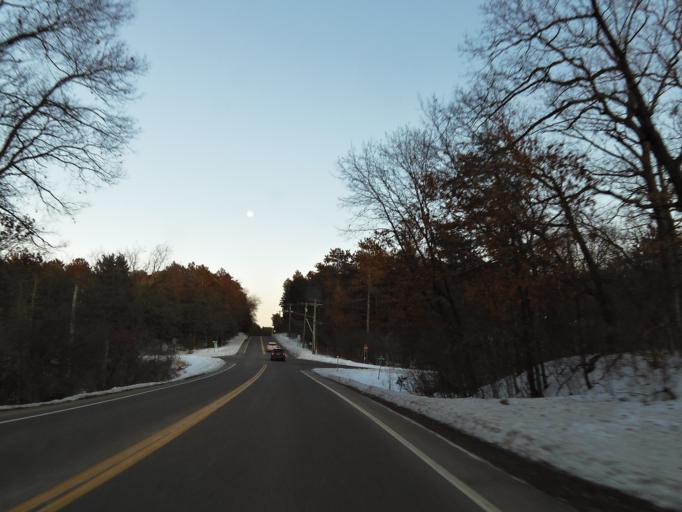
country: US
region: Minnesota
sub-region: Washington County
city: Dellwood
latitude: 45.0886
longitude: -92.9542
